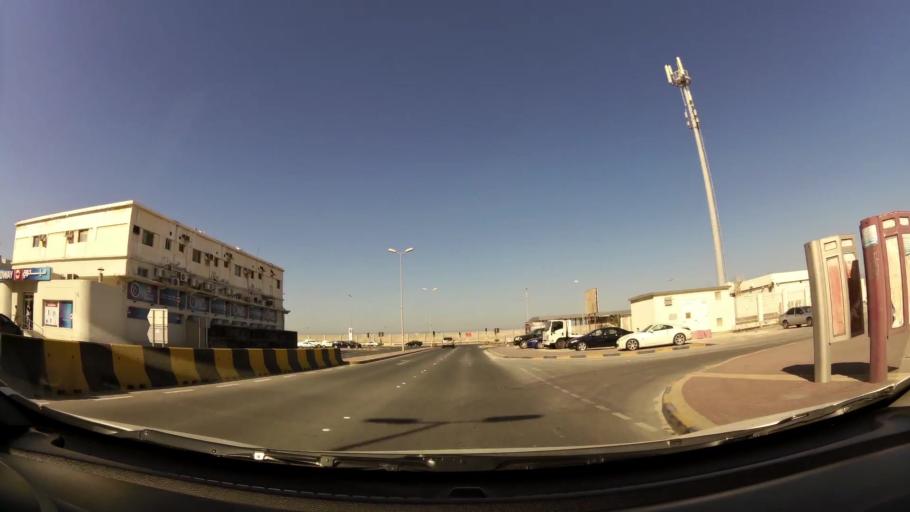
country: BH
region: Muharraq
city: Al Hadd
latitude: 26.2564
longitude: 50.6487
